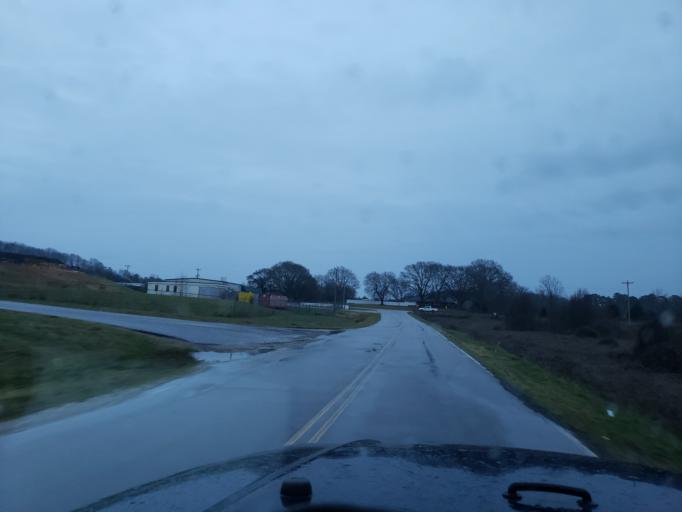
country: US
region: South Carolina
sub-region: Cherokee County
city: Blacksburg
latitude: 35.1565
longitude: -81.4528
